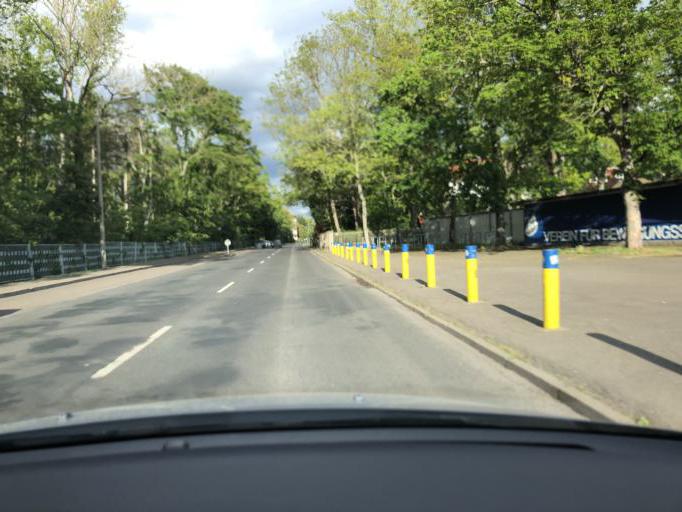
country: DE
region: Saxony
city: Markkleeberg
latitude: 51.3045
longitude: 12.4189
